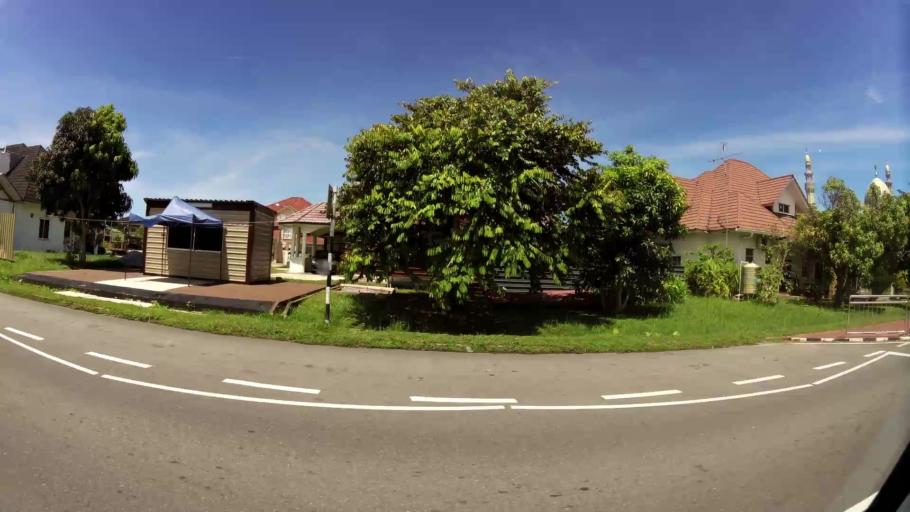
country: BN
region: Belait
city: Kuala Belait
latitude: 4.5878
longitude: 114.2314
